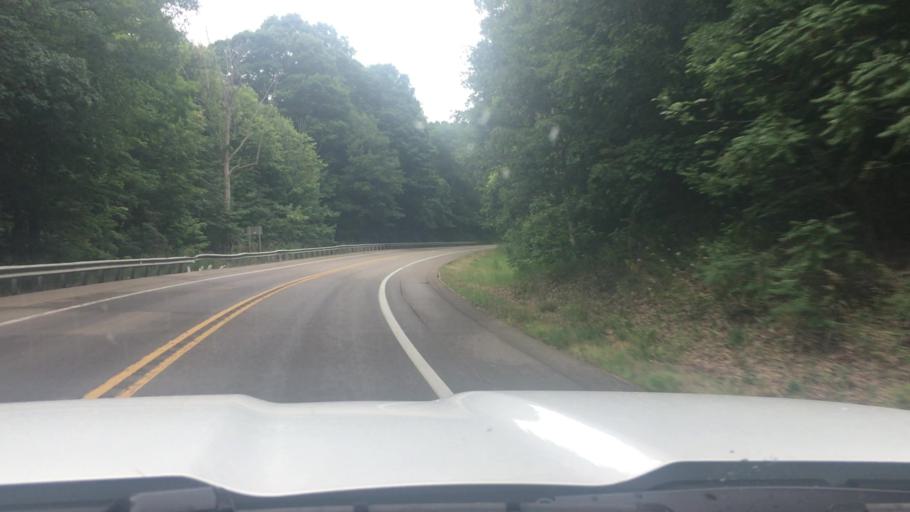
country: US
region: Michigan
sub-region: Ionia County
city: Ionia
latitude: 42.9732
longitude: -85.1256
